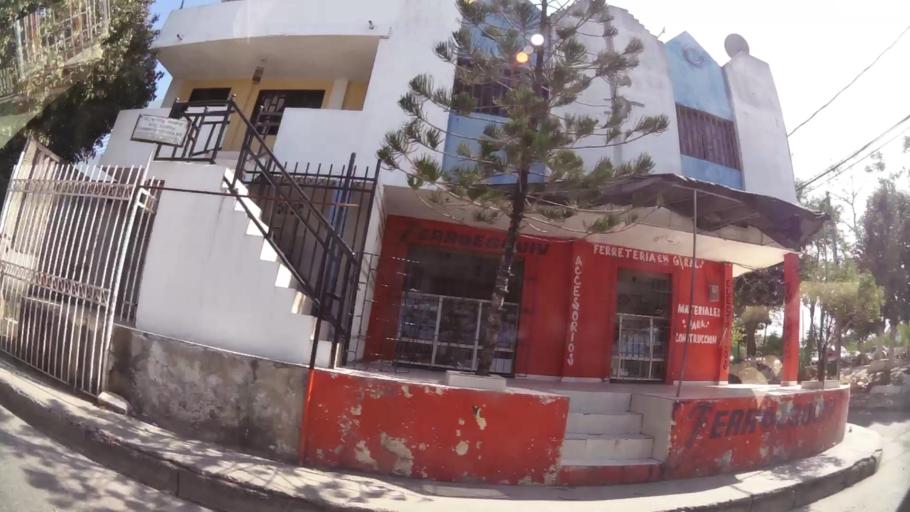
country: CO
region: Bolivar
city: Cartagena
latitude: 10.3783
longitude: -75.4665
